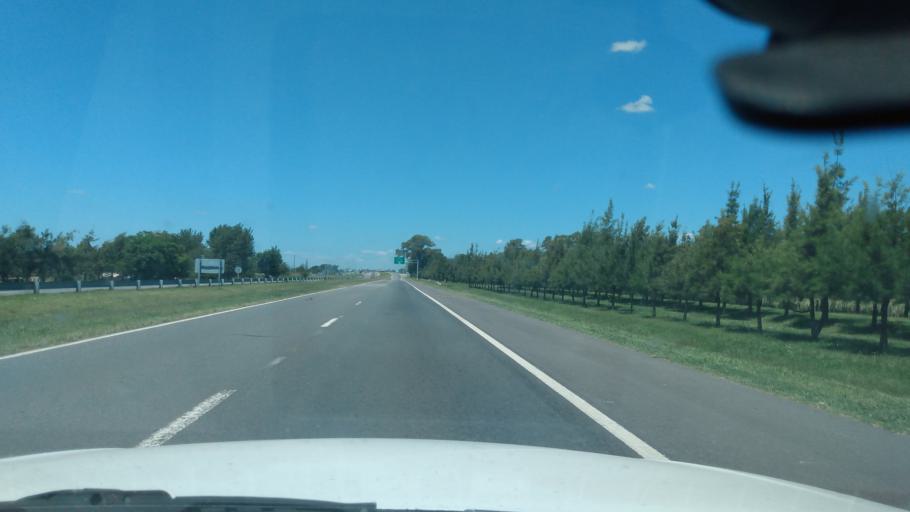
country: AR
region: Buenos Aires
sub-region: Partido de San Andres de Giles
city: San Andres de Giles
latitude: -34.5001
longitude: -59.3423
